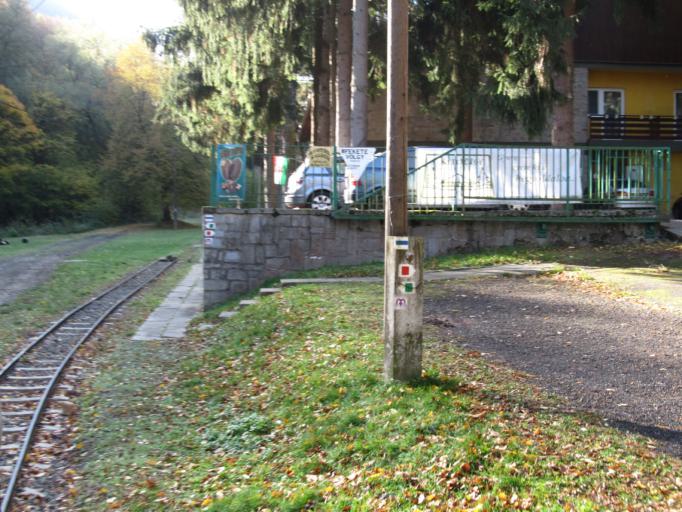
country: SK
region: Nitriansky
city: Sahy
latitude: 47.9832
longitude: 18.8970
